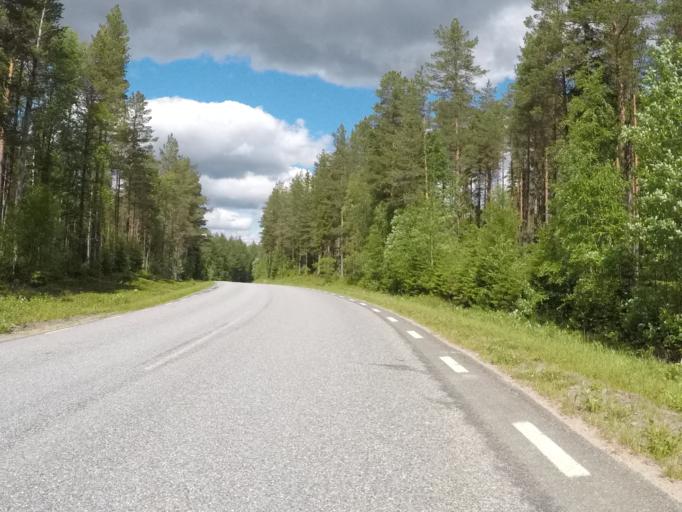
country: SE
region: Vaesterbotten
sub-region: Robertsfors Kommun
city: Robertsfors
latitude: 63.9783
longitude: 20.8107
